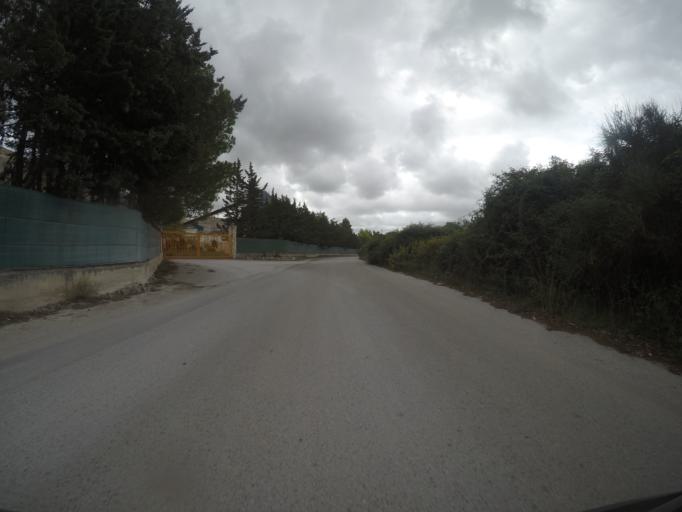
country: IT
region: Sicily
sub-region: Palermo
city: Montelepre
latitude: 38.1052
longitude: 13.1708
